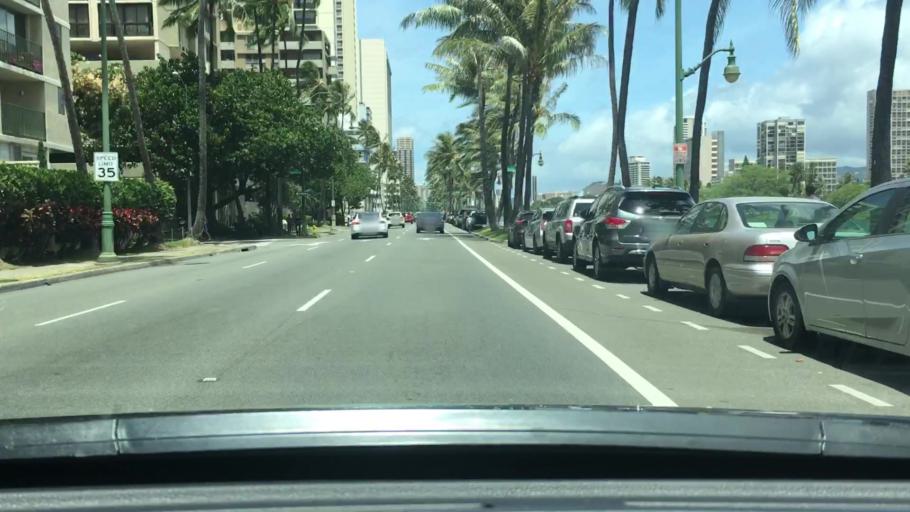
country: US
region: Hawaii
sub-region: Honolulu County
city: Honolulu
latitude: 21.2795
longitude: -157.8233
